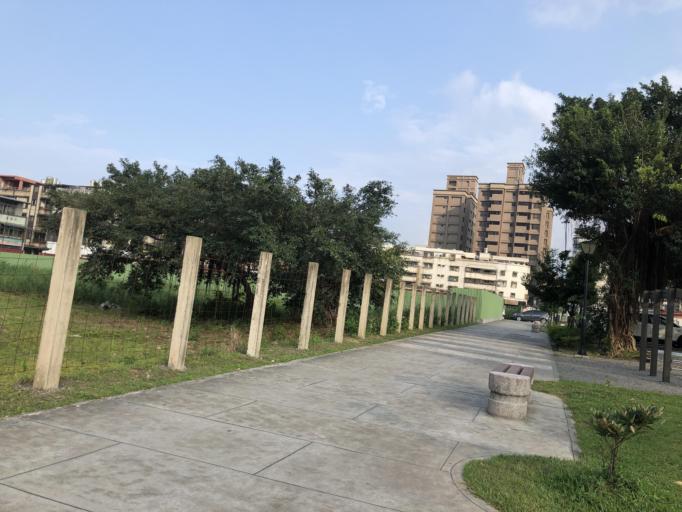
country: TW
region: Taiwan
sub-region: Keelung
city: Keelung
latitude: 25.2206
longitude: 121.6367
